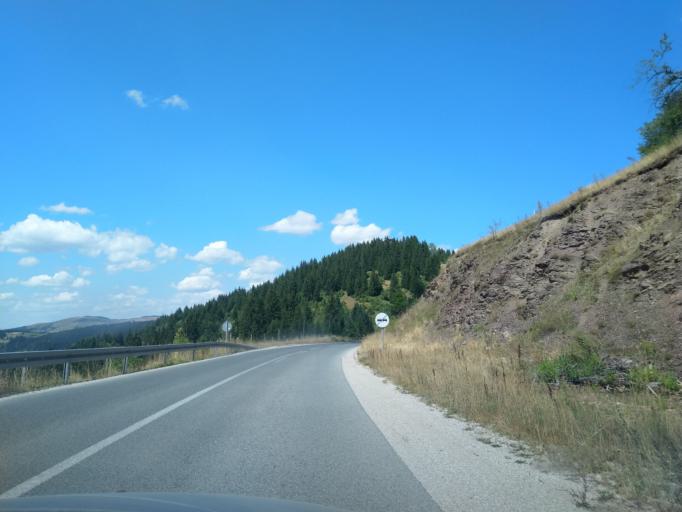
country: RS
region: Central Serbia
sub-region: Zlatiborski Okrug
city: Nova Varos
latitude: 43.4299
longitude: 19.8279
